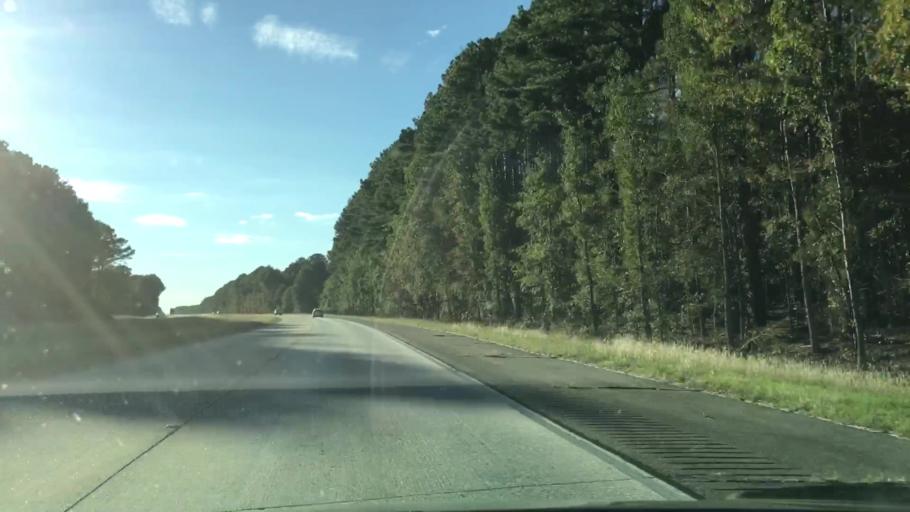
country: US
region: Georgia
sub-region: Greene County
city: Greensboro
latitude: 33.5496
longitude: -83.1306
